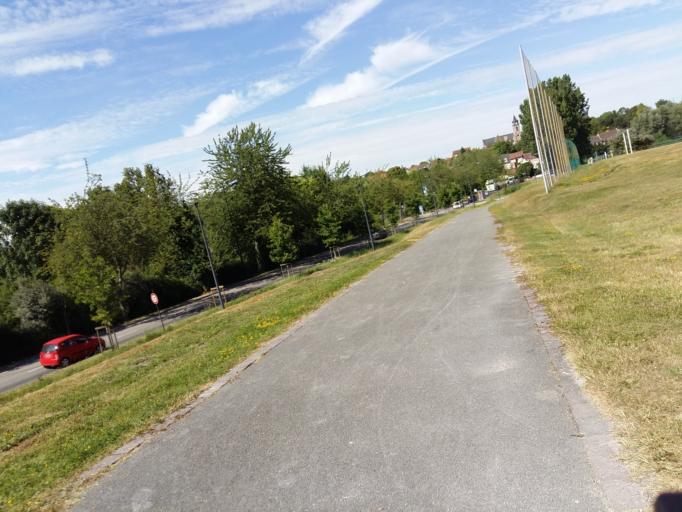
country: FR
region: Picardie
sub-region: Departement de la Somme
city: Dreuil-les-Amiens
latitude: 49.9196
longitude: 2.2592
